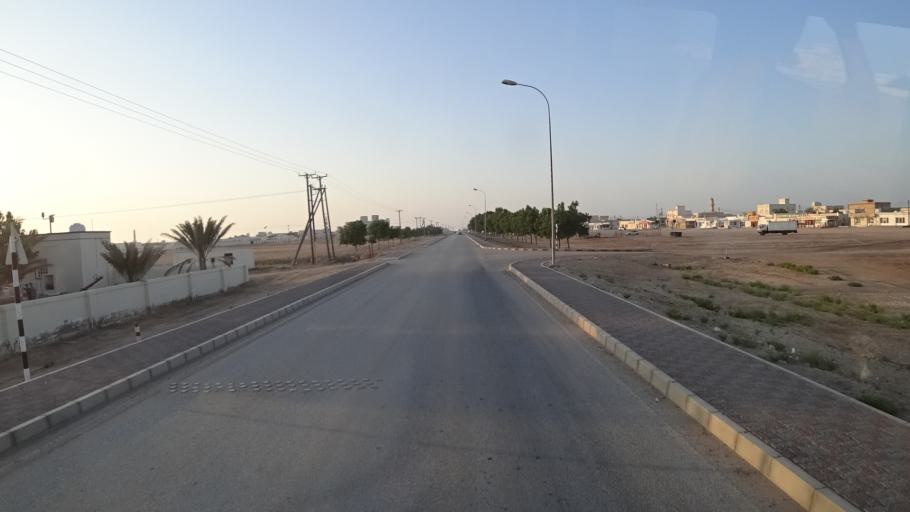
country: OM
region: Ash Sharqiyah
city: Sur
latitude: 22.5170
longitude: 59.7931
